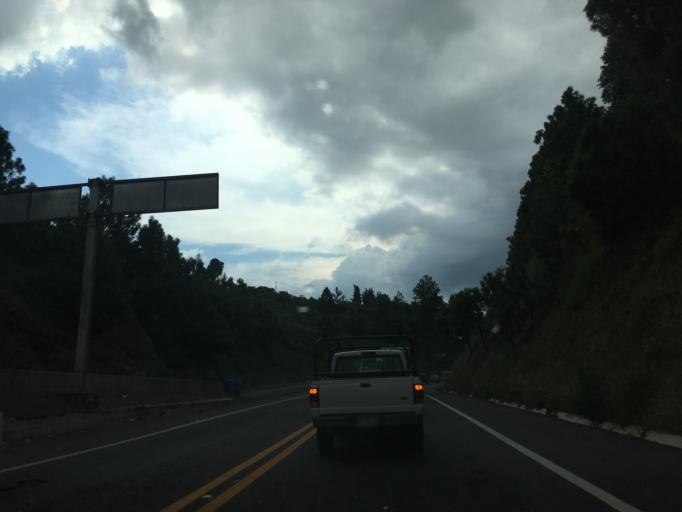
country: MX
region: Michoacan
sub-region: Uruapan
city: Toreo Bajo (El Toreo Bajo)
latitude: 19.4193
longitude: -101.9938
